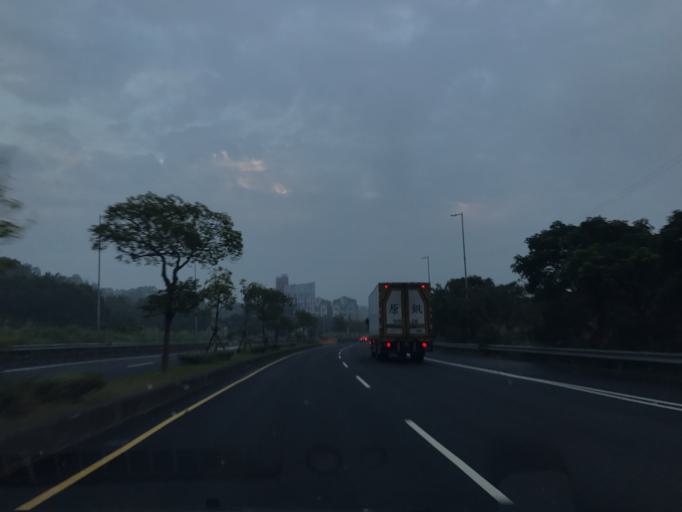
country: TW
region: Taiwan
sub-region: Hsinchu
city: Hsinchu
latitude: 24.7634
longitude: 120.9577
